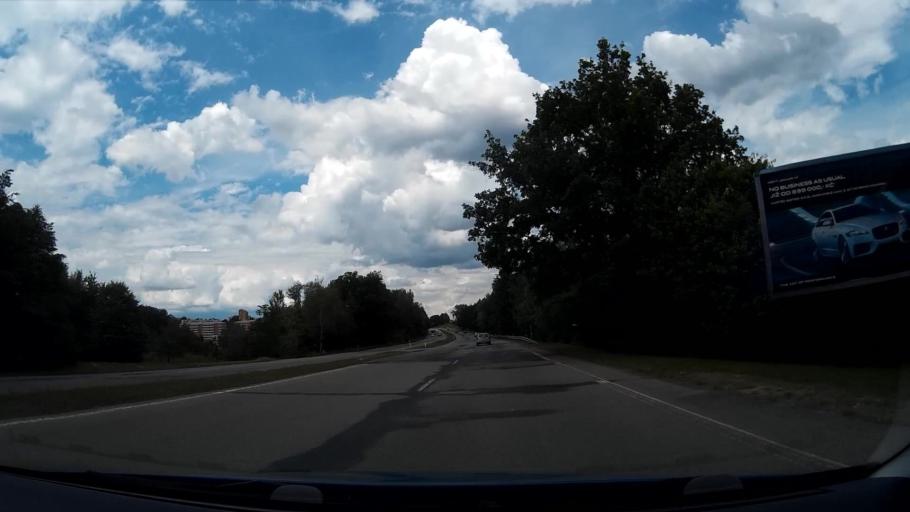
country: CZ
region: South Moravian
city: Troubsko
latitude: 49.2113
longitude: 16.5217
